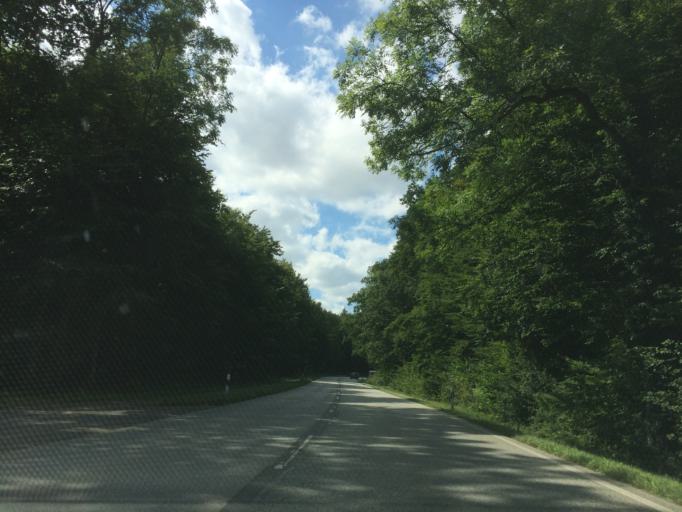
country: DE
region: Schleswig-Holstein
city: Malente
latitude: 54.1320
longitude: 10.5601
